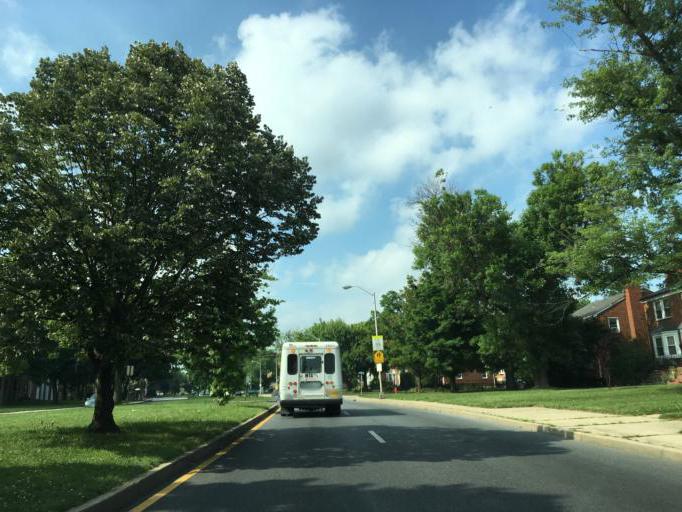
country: US
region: Maryland
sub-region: Baltimore County
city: Towson
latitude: 39.3540
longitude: -76.5898
